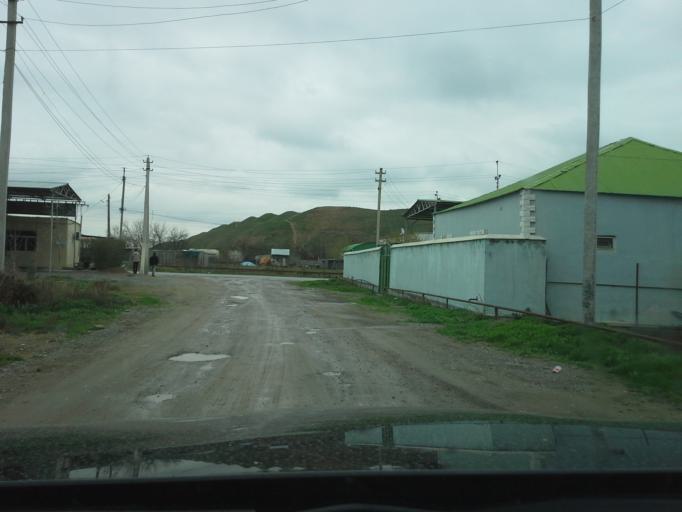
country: TM
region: Ahal
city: Abadan
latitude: 37.9495
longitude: 58.2061
